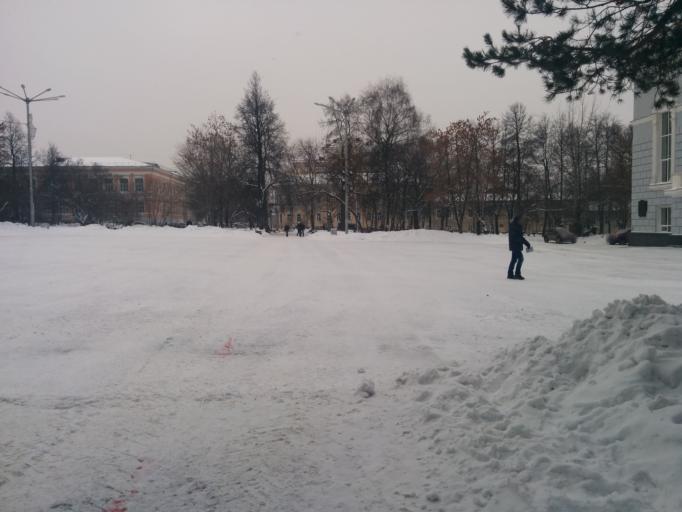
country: RU
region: Perm
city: Perm
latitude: 58.0156
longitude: 56.2468
